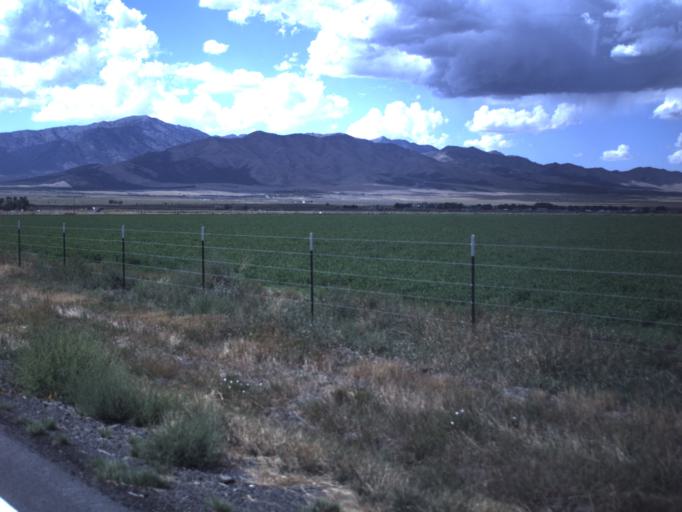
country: US
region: Utah
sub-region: Tooele County
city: Tooele
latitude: 40.3368
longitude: -112.4317
